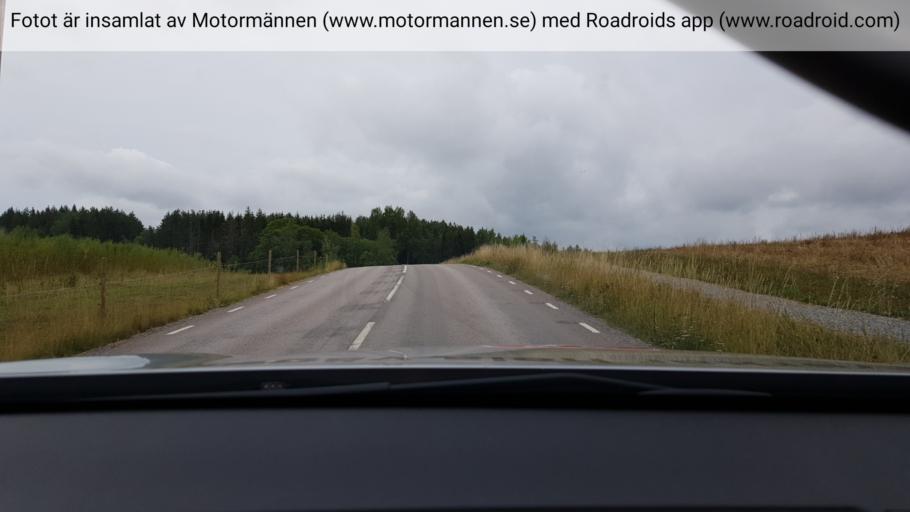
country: SE
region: Soedermanland
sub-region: Gnesta Kommun
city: Gnesta
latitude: 59.0631
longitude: 17.2948
